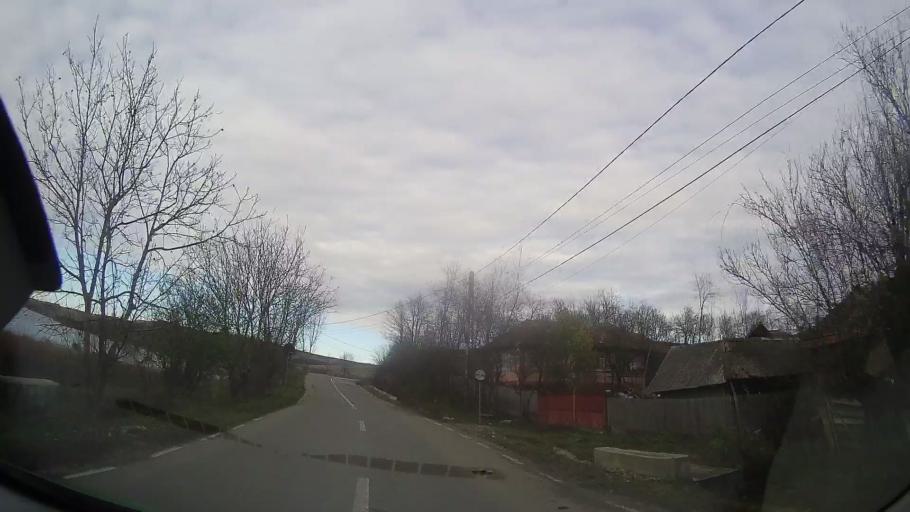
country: RO
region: Cluj
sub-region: Comuna Geaca
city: Geaca
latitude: 46.8380
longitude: 24.1344
